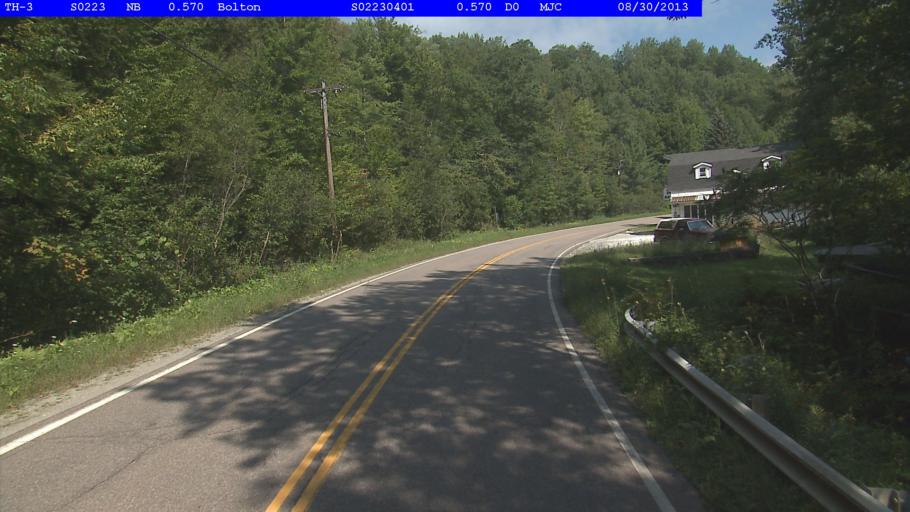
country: US
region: Vermont
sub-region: Washington County
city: Waterbury
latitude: 44.3793
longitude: -72.8763
